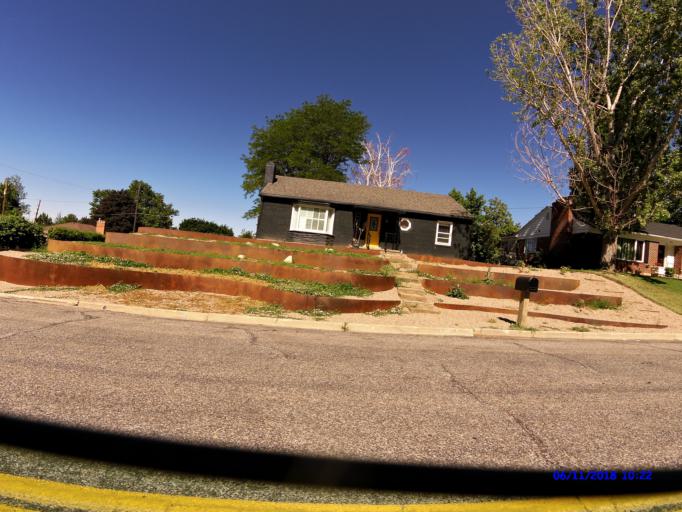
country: US
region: Utah
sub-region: Weber County
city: South Ogden
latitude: 41.2073
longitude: -111.9414
